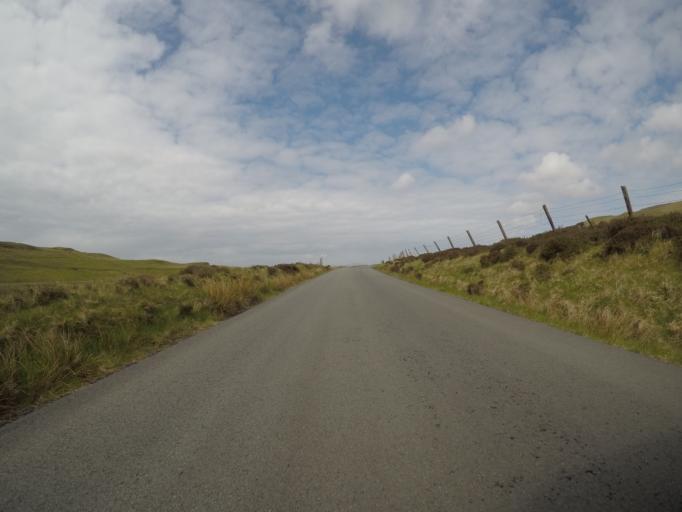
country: GB
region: Scotland
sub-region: Highland
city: Portree
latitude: 57.5970
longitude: -6.3754
